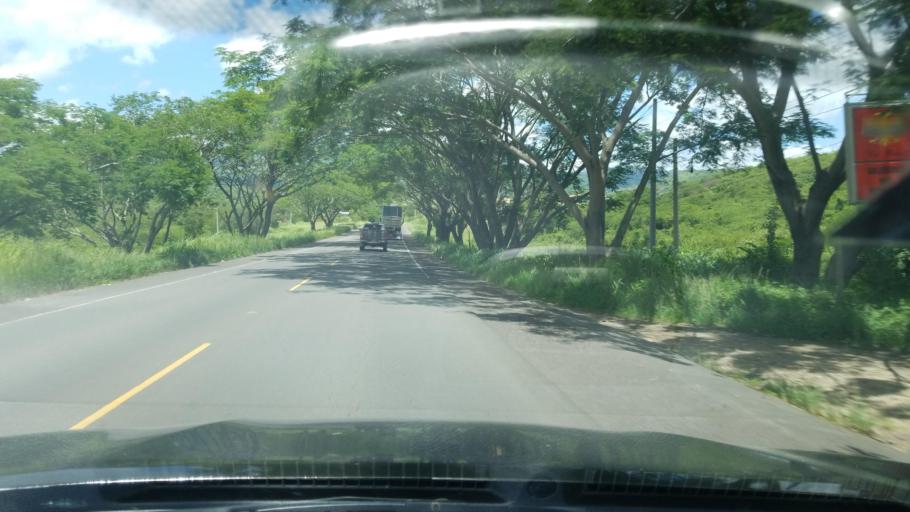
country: HN
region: Francisco Morazan
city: Cofradia
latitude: 14.2713
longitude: -87.2440
